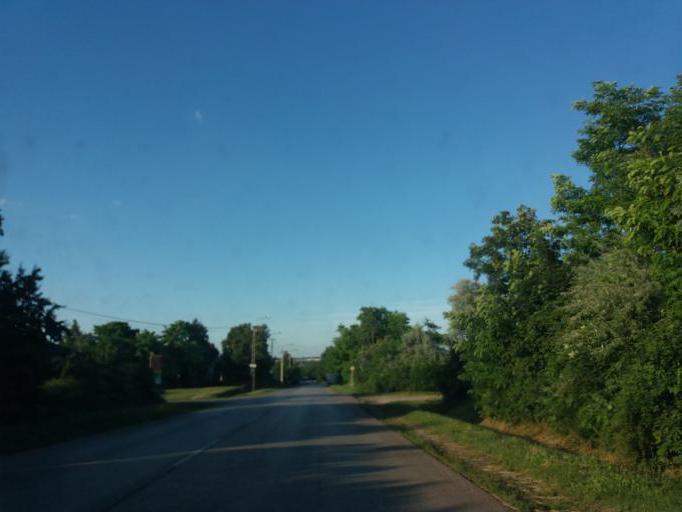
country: HU
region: Fejer
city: Martonvasar
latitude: 47.3048
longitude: 18.7795
